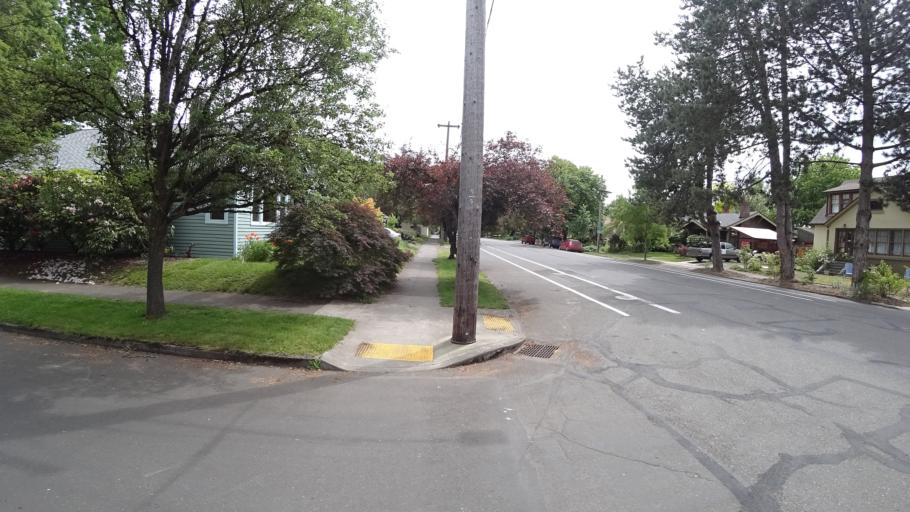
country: US
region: Oregon
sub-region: Clackamas County
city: Milwaukie
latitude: 45.4814
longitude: -122.6205
